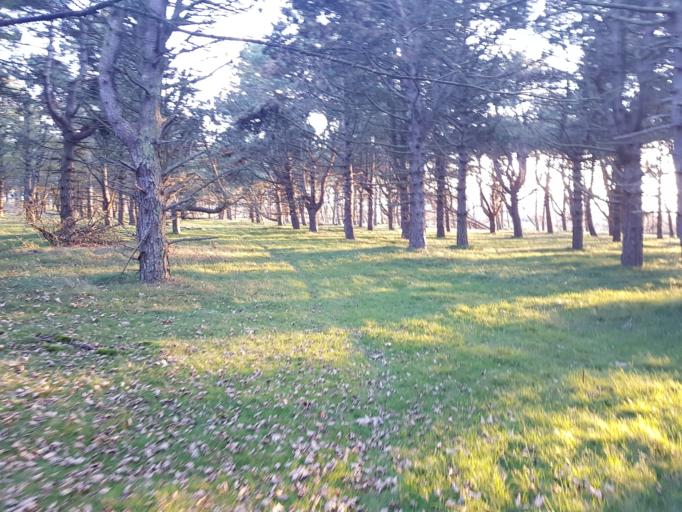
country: NL
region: South Holland
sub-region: Gemeente Noordwijkerhout
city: Noordwijkerhout
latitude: 52.3161
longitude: 4.5104
